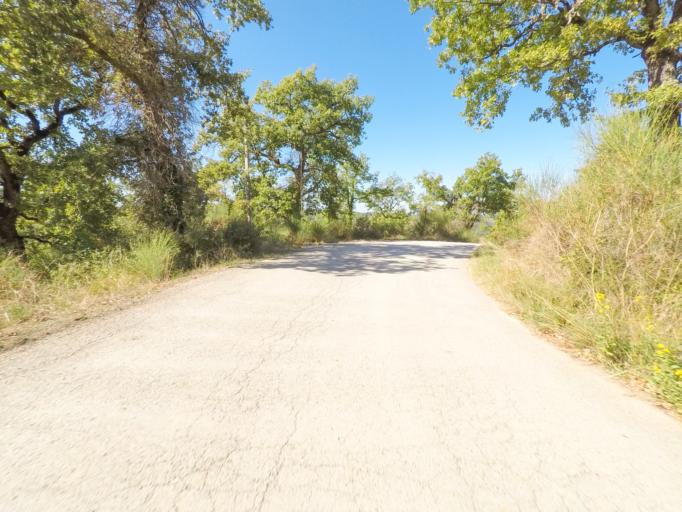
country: IT
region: Tuscany
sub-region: Provincia di Siena
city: Castellina in Chianti
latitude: 43.4372
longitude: 11.3256
